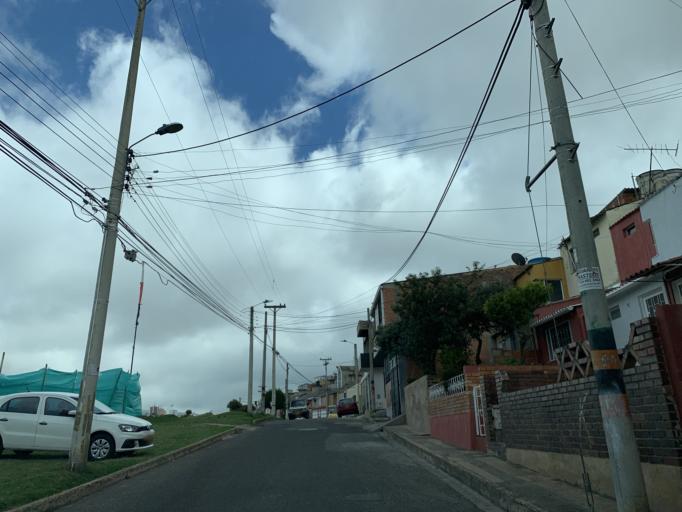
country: CO
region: Boyaca
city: Tunja
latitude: 5.5484
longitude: -73.3628
